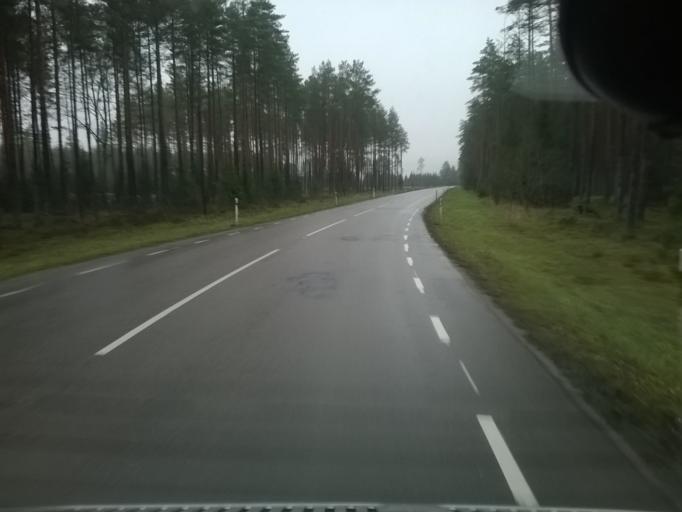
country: EE
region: Harju
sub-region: Saku vald
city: Saku
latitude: 59.2521
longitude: 24.6891
